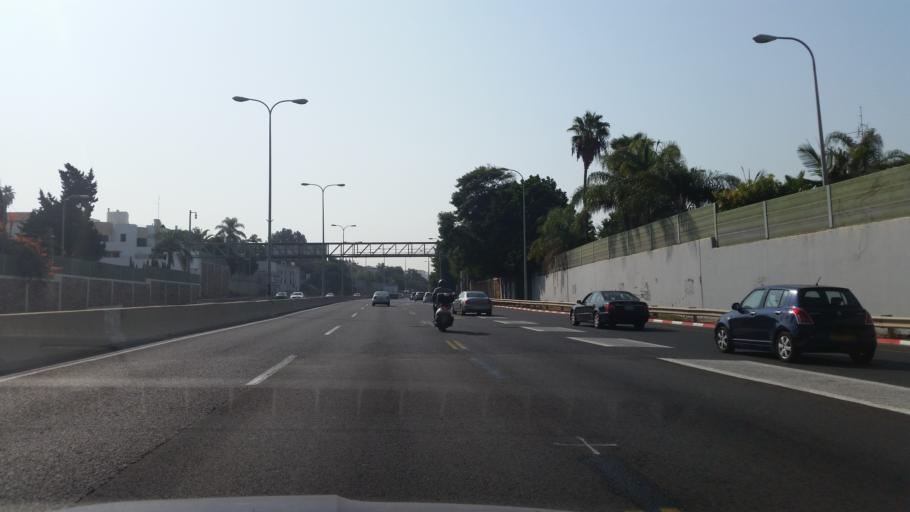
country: IL
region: Tel Aviv
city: Kefar Shemaryahu
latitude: 32.1760
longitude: 34.8159
